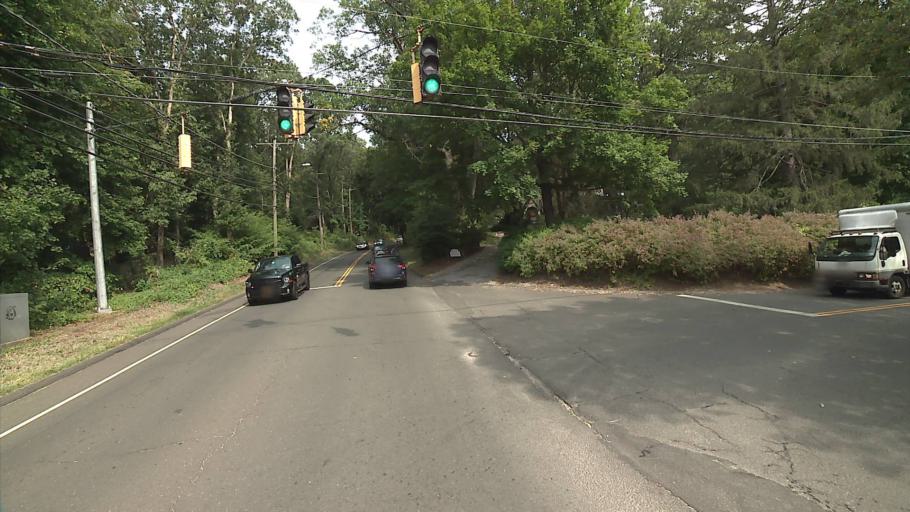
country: US
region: Connecticut
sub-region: Fairfield County
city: North Stamford
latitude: 41.1254
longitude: -73.5445
